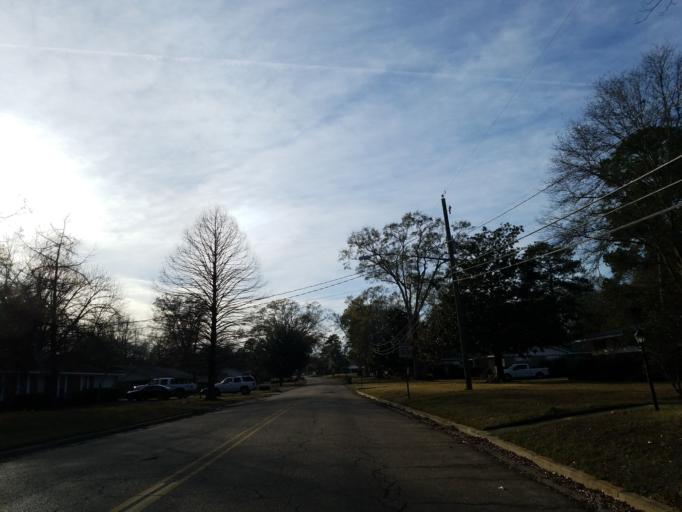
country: US
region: Mississippi
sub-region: Lamar County
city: West Hattiesburg
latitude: 31.3133
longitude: -89.3318
